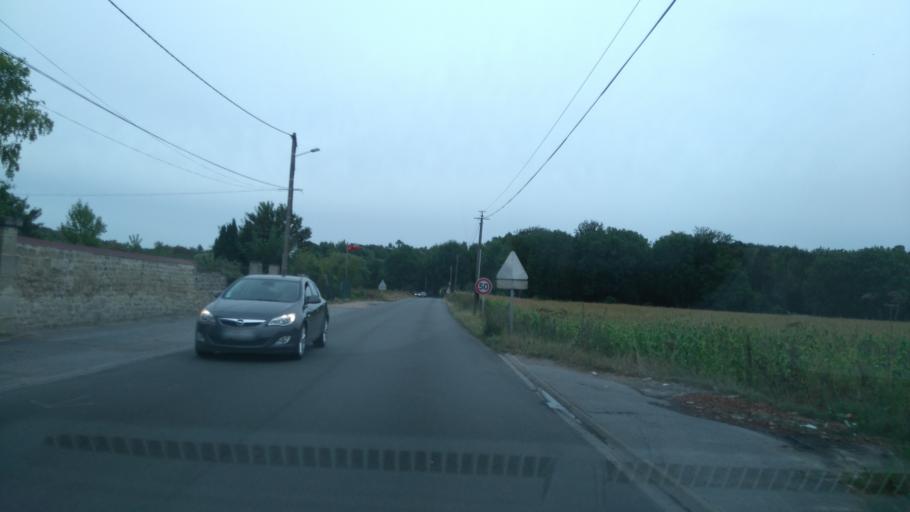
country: FR
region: Picardie
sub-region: Departement de l'Oise
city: Gouvieux
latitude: 49.2131
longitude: 2.4242
